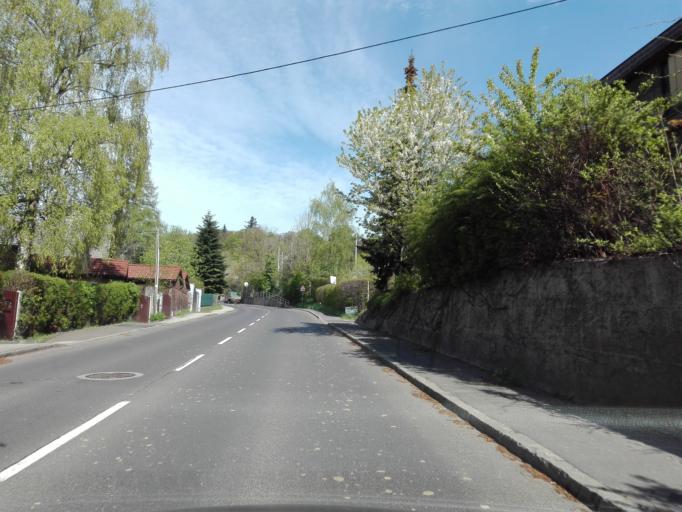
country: AT
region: Upper Austria
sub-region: Linz Stadt
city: Linz
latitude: 48.3145
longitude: 14.2599
